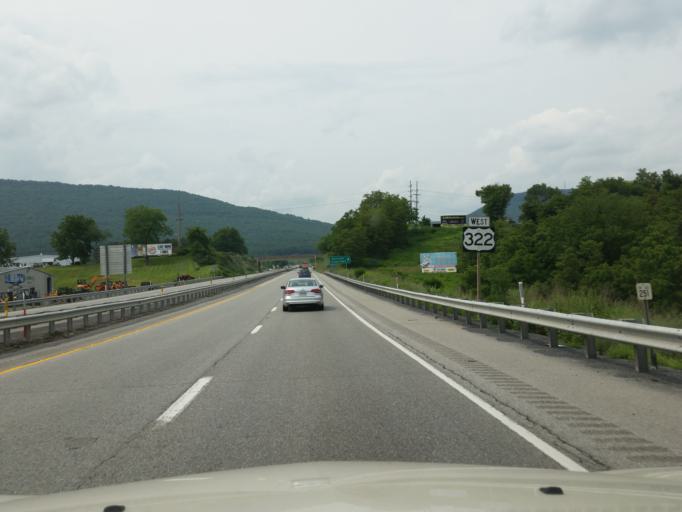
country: US
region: Pennsylvania
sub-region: Mifflin County
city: Highland Park
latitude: 40.6255
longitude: -77.5818
